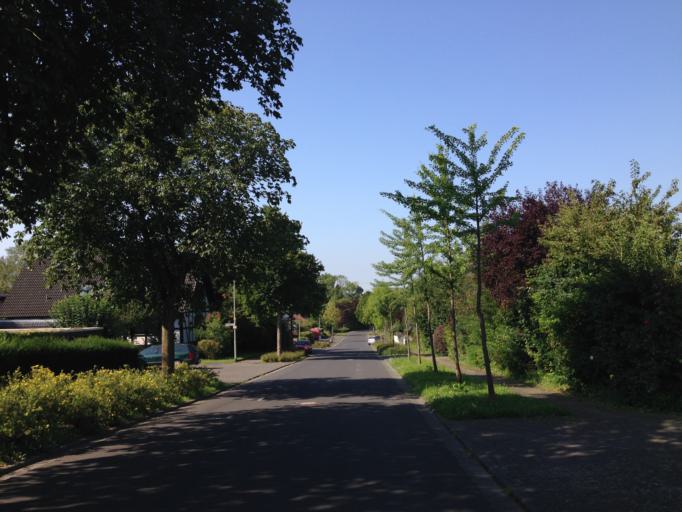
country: DE
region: Hesse
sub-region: Regierungsbezirk Giessen
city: Langgons
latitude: 50.5216
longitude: 8.6807
